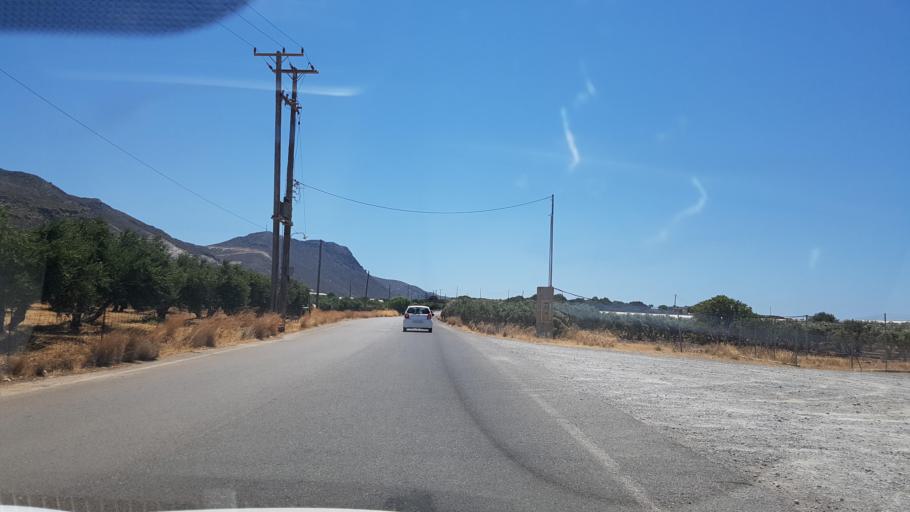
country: GR
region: Crete
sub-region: Nomos Chanias
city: Palaiochora
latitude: 35.2903
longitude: 23.5466
